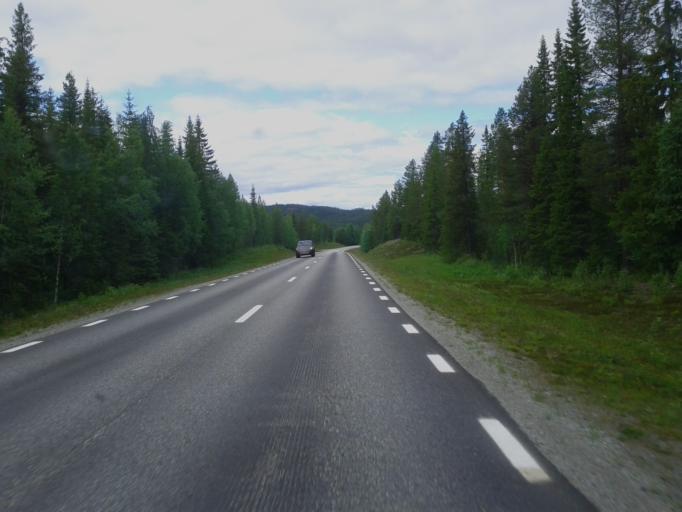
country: SE
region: Vaesterbotten
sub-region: Storumans Kommun
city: Fristad
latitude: 65.3588
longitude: 16.5453
